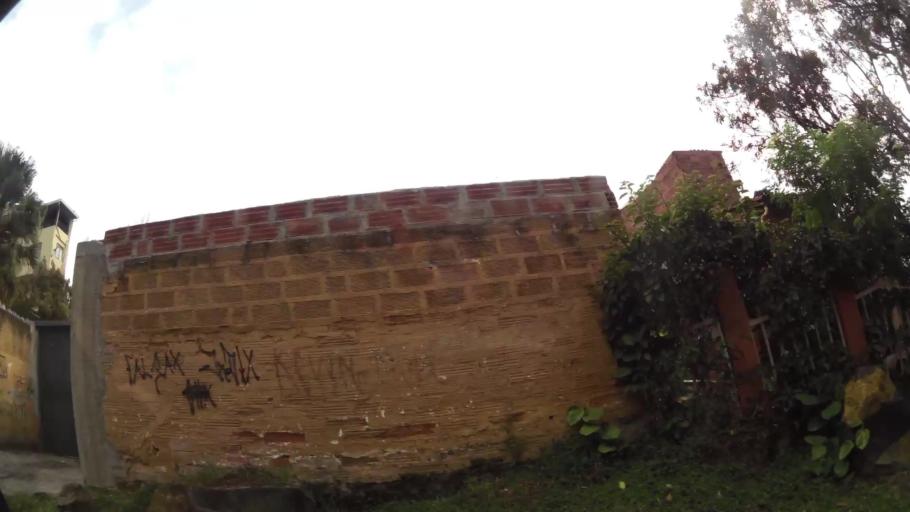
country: CO
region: Antioquia
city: Medellin
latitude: 6.2801
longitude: -75.5992
